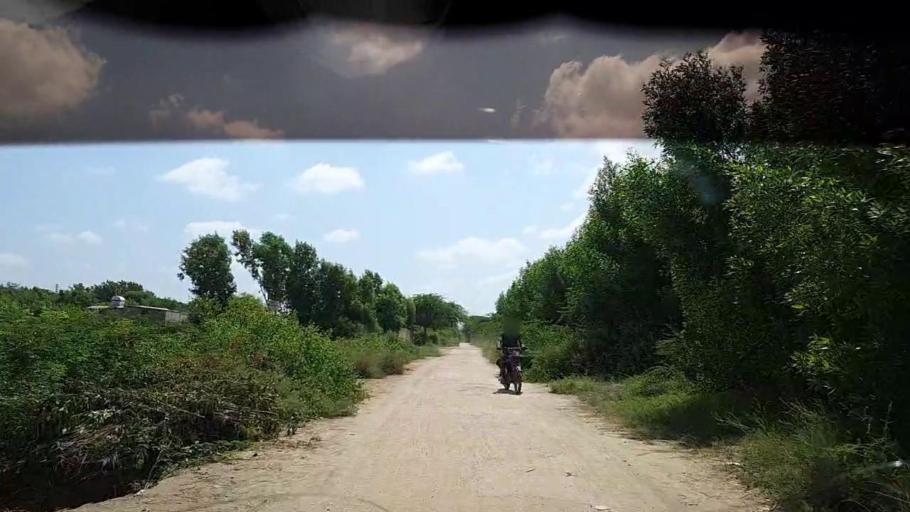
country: PK
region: Sindh
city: Kadhan
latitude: 24.5894
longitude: 68.9581
